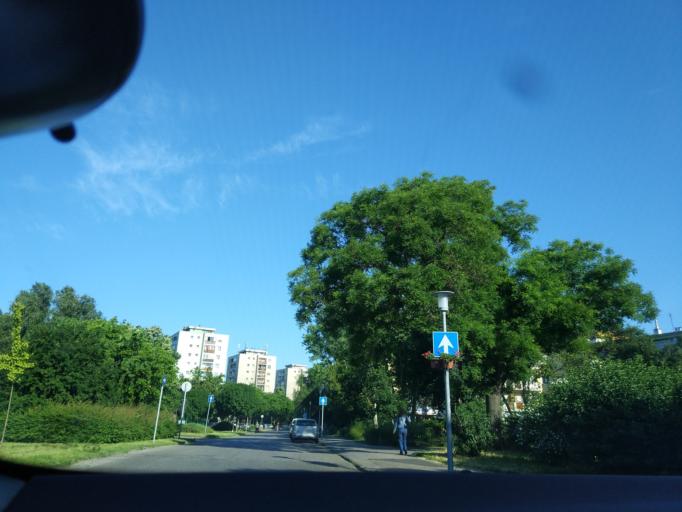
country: HU
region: Budapest
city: Budapest XX. keruelet
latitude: 47.4654
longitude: 19.1153
